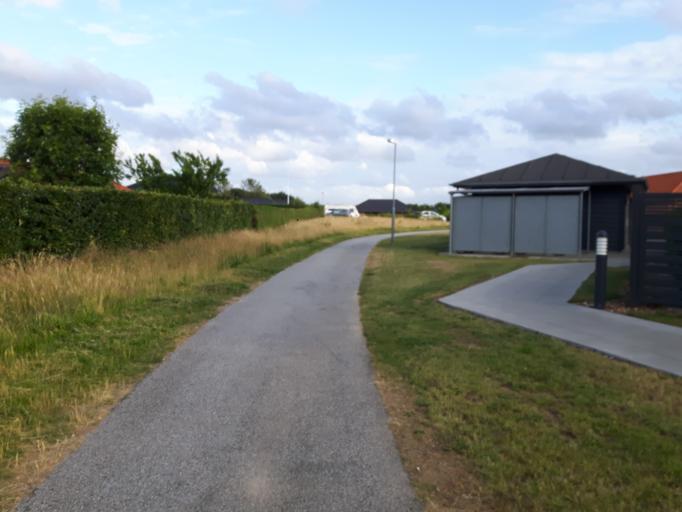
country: DK
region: Central Jutland
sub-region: Skive Kommune
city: Skive
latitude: 56.5517
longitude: 9.0520
